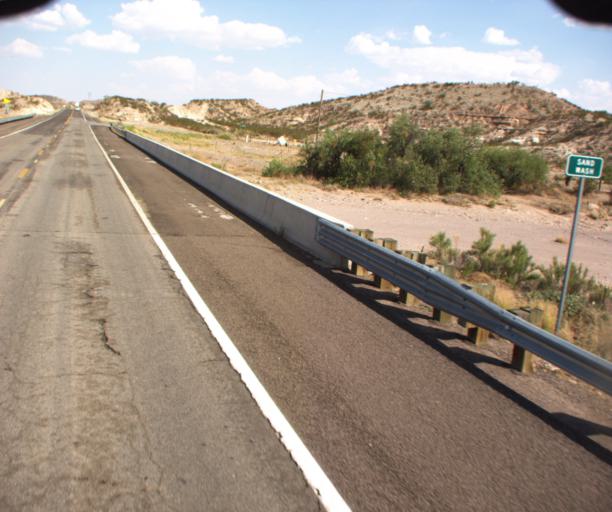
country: US
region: Arizona
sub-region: Greenlee County
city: Clifton
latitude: 32.7655
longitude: -109.1463
